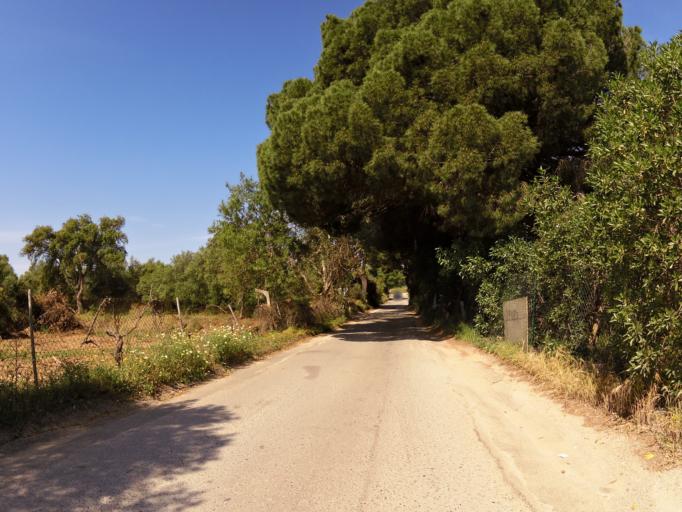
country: PT
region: Faro
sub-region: Loule
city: Almancil
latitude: 37.0699
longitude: -8.0045
